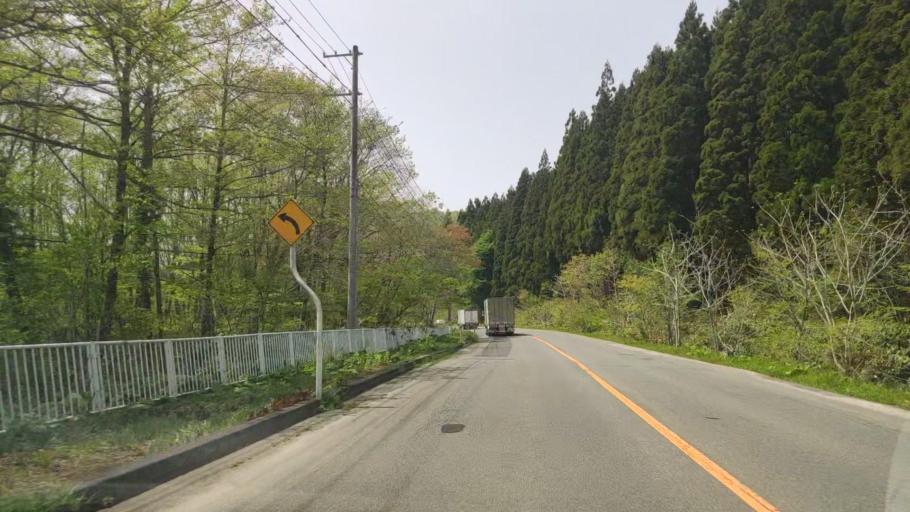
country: JP
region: Aomori
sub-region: Misawa Shi
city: Inuotose
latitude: 40.7909
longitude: 141.0962
